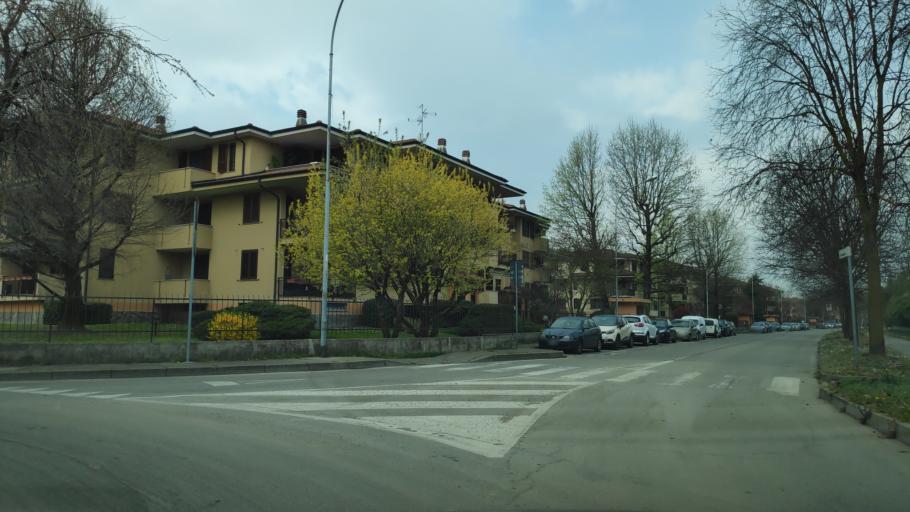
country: IT
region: Lombardy
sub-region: Citta metropolitana di Milano
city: Liscate
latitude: 45.4769
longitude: 9.4117
